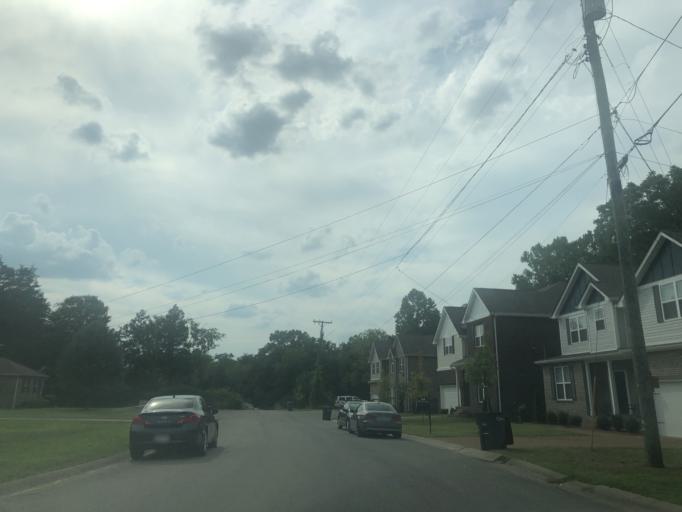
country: US
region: Tennessee
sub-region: Wilson County
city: Green Hill
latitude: 36.1808
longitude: -86.5856
